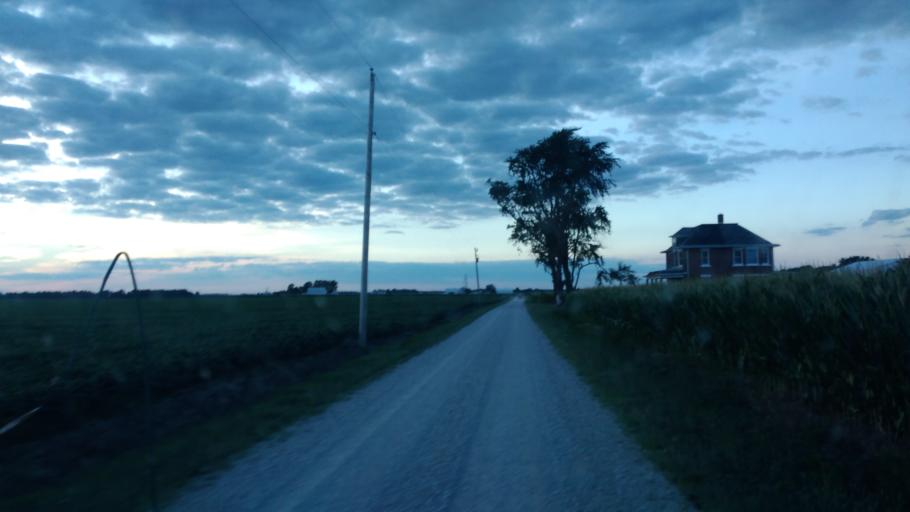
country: US
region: Indiana
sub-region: Adams County
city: Berne
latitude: 40.6452
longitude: -85.0796
